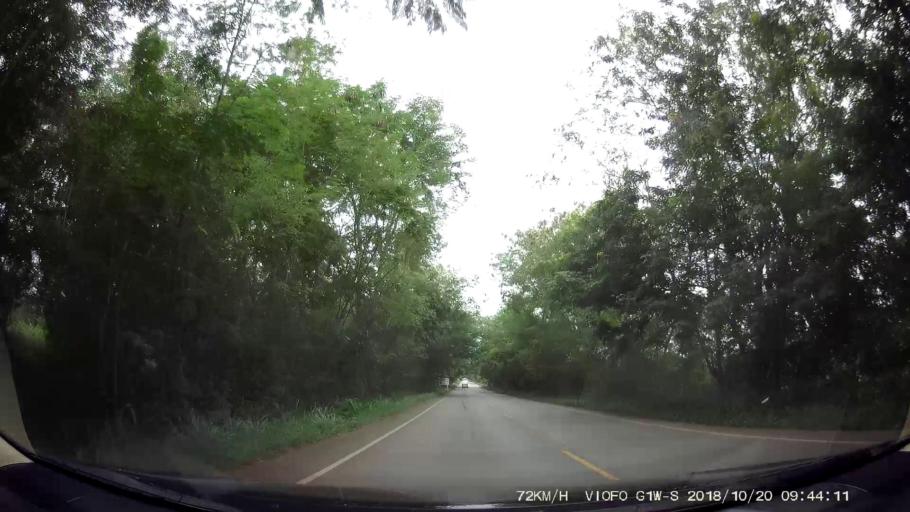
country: TH
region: Chaiyaphum
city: Khon San
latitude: 16.4806
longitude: 101.9450
